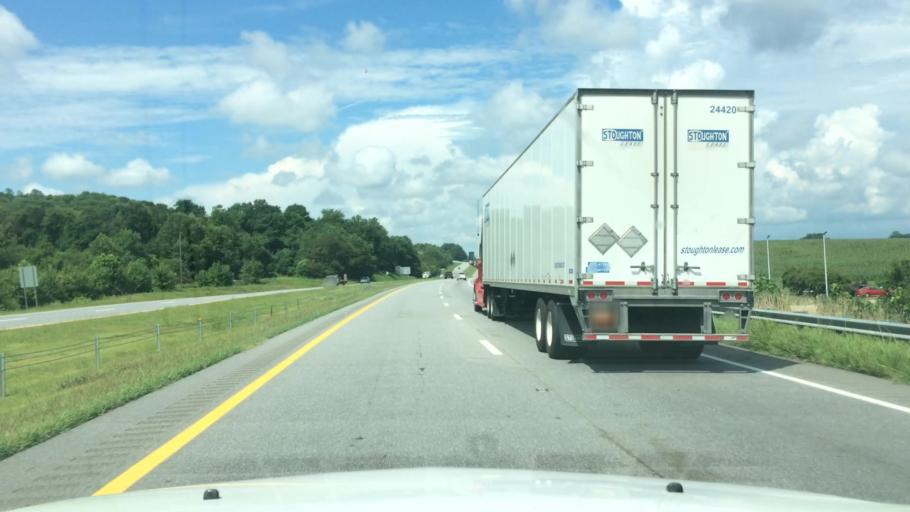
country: US
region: North Carolina
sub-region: Wilkes County
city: North Wilkesboro
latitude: 36.1513
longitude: -81.0025
